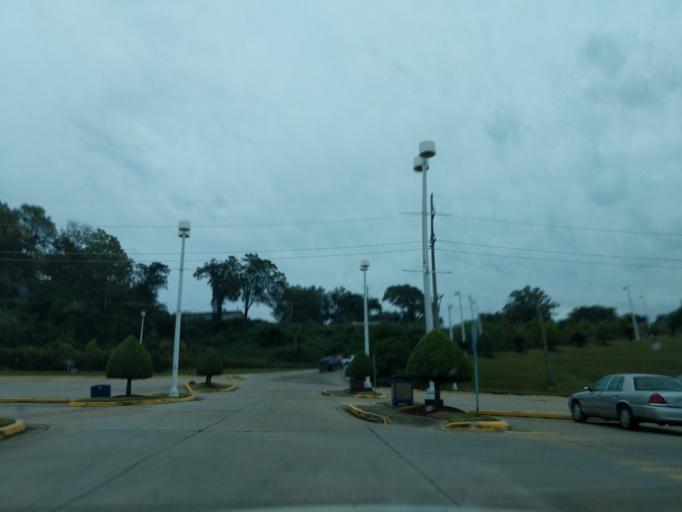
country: US
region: Mississippi
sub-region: Warren County
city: Vicksburg
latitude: 32.3249
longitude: -90.8959
